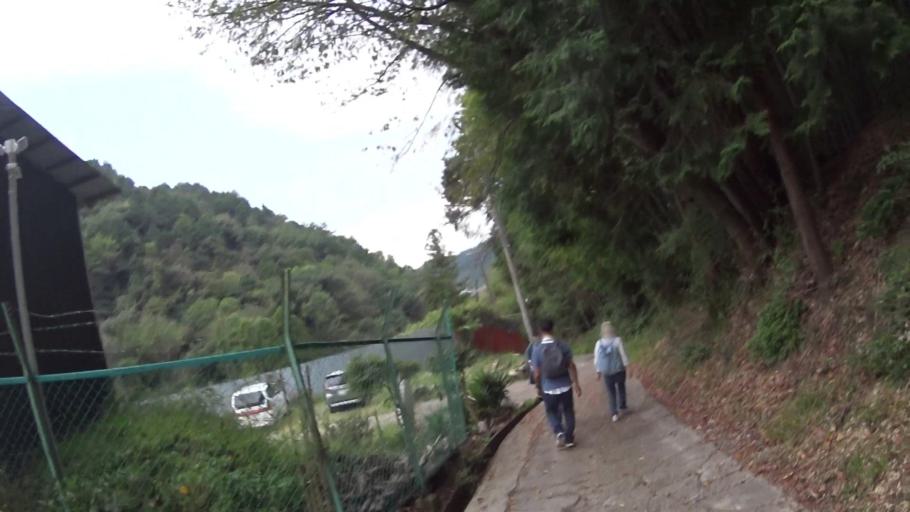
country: JP
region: Osaka
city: Kaizuka
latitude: 34.4657
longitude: 135.2983
